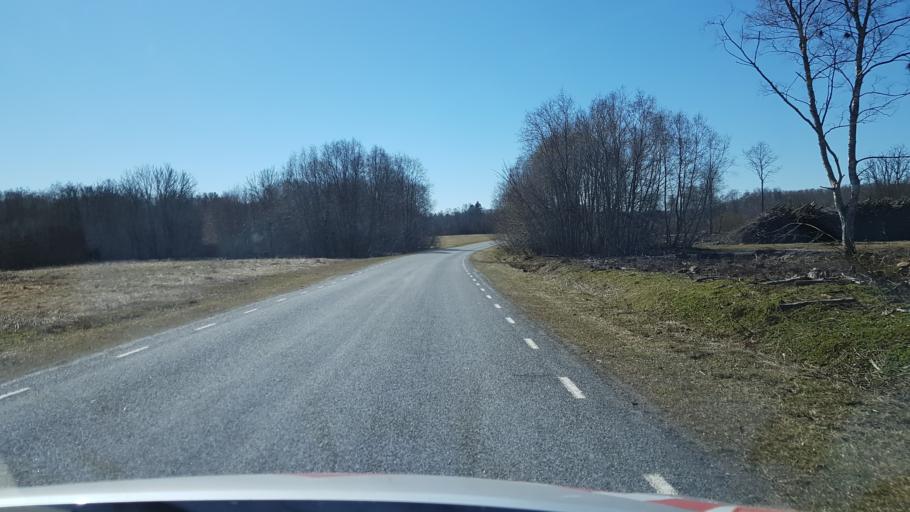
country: EE
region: Laeaene-Virumaa
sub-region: Haljala vald
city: Haljala
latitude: 59.5252
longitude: 26.2360
